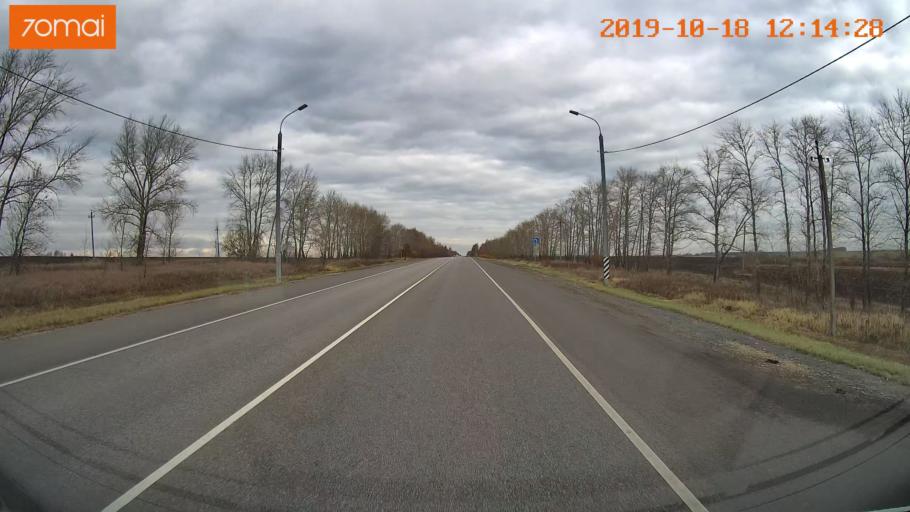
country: RU
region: Rjazan
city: Zakharovo
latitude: 54.4312
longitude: 39.3837
